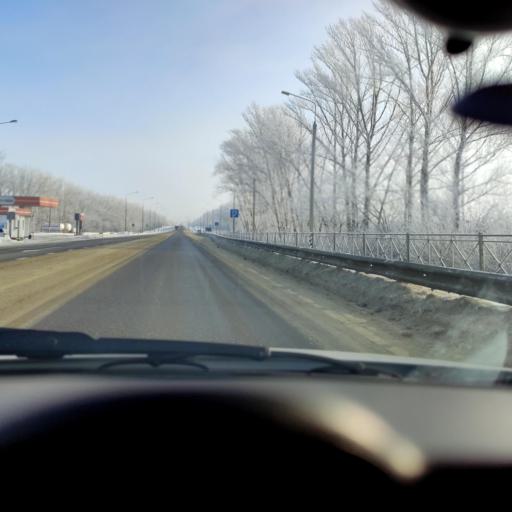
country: RU
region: Belgorod
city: Troitskiy
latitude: 51.6182
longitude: 37.5343
